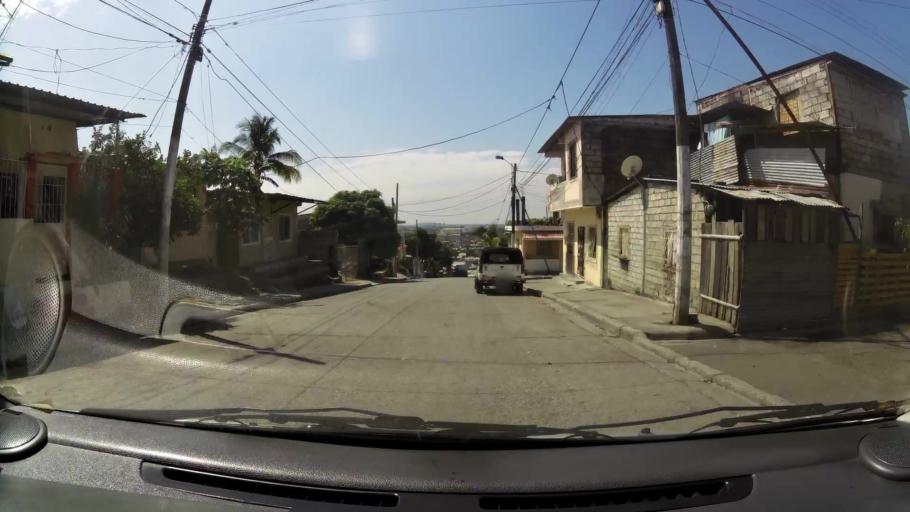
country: EC
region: Guayas
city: Eloy Alfaro
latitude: -2.1288
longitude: -79.9150
